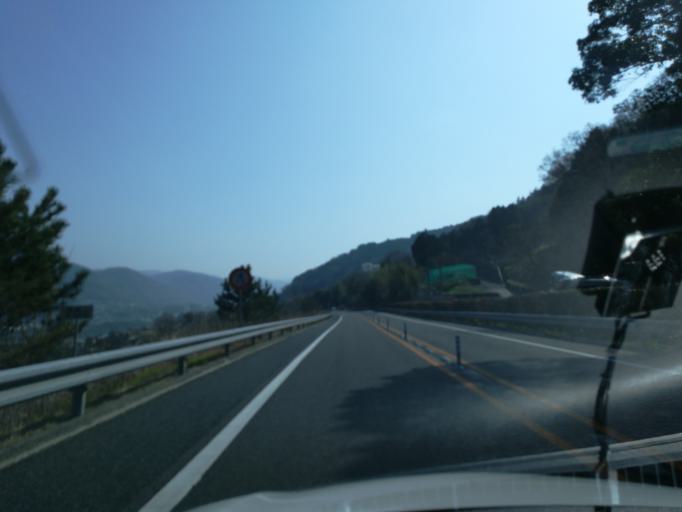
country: JP
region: Tokushima
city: Ikedacho
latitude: 34.0253
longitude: 133.8223
